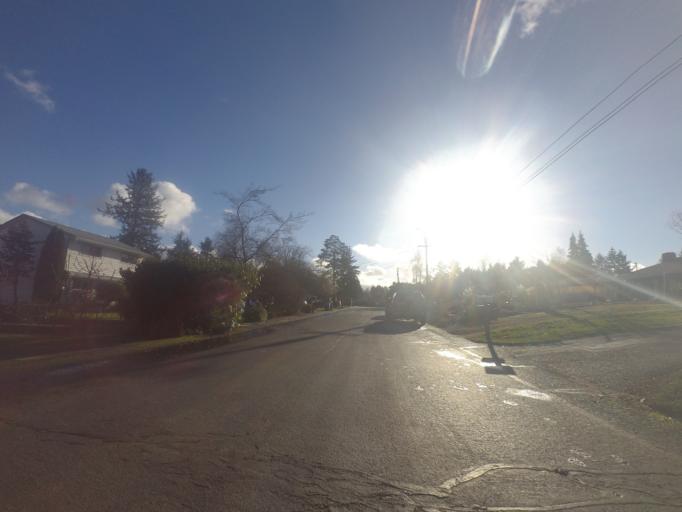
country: US
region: Washington
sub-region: Pierce County
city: University Place
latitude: 47.2273
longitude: -122.5415
